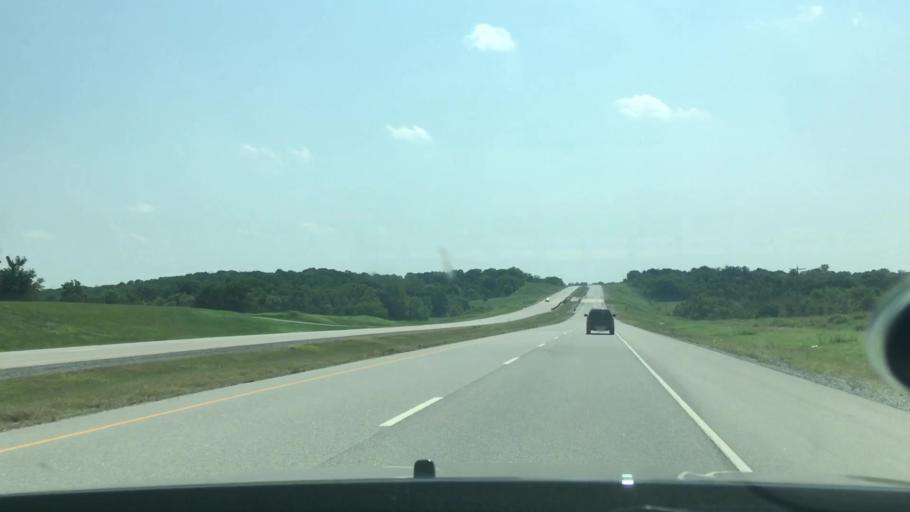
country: US
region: Oklahoma
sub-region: Atoka County
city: Atoka
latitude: 34.3561
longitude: -96.0906
